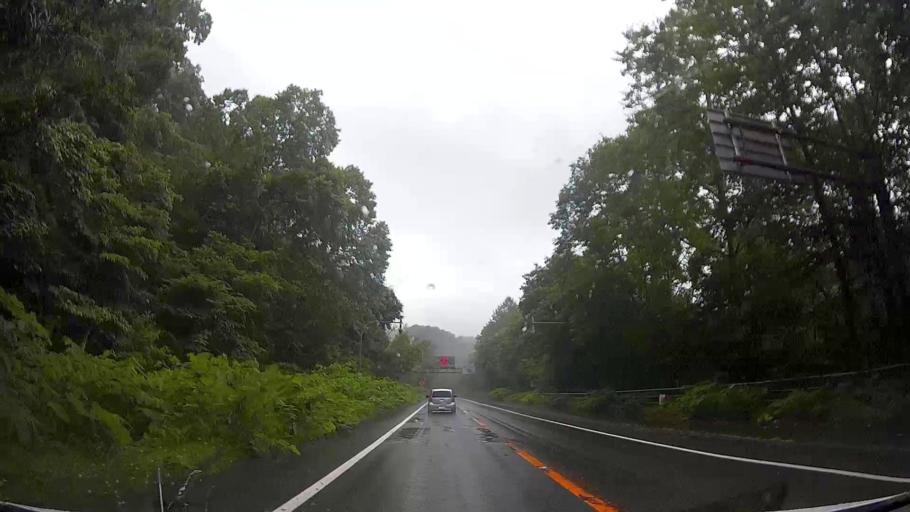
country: JP
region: Hokkaido
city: Shiraoi
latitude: 42.7209
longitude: 141.2600
